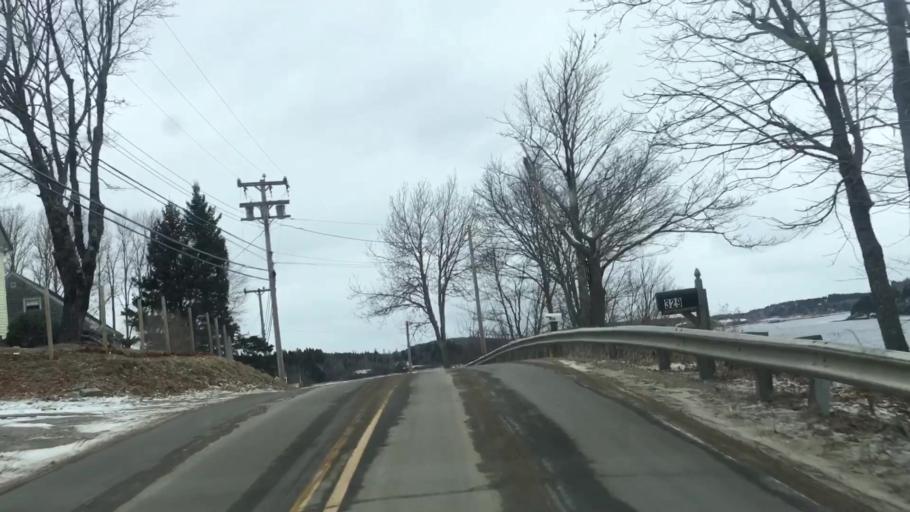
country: US
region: Maine
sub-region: Washington County
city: Machiasport
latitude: 44.6979
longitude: -67.3939
